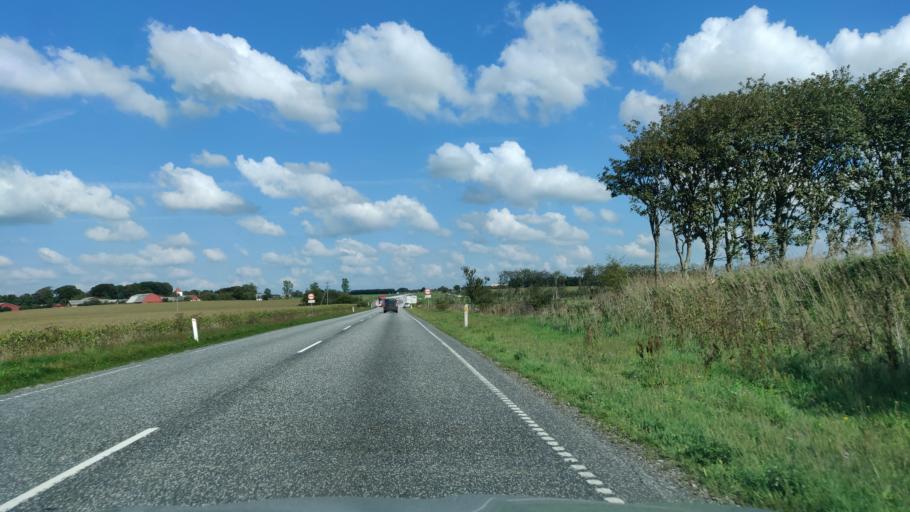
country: DK
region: North Denmark
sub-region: Vesthimmerland Kommune
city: Aars
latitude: 56.8054
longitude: 9.6467
